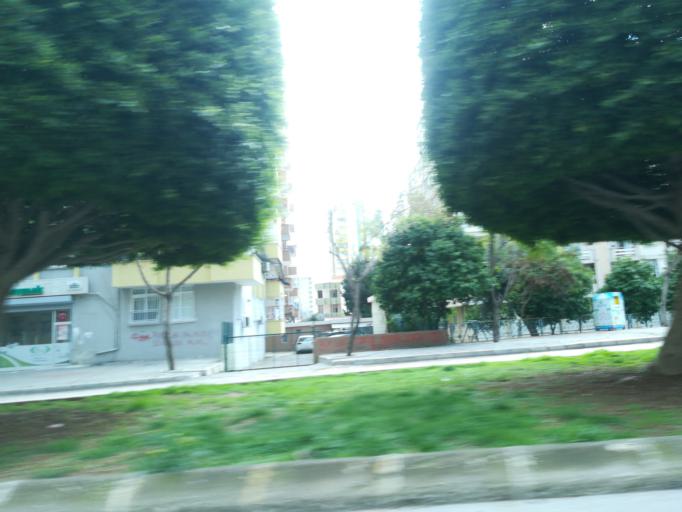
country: TR
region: Adana
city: Adana
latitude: 37.0310
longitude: 35.3034
